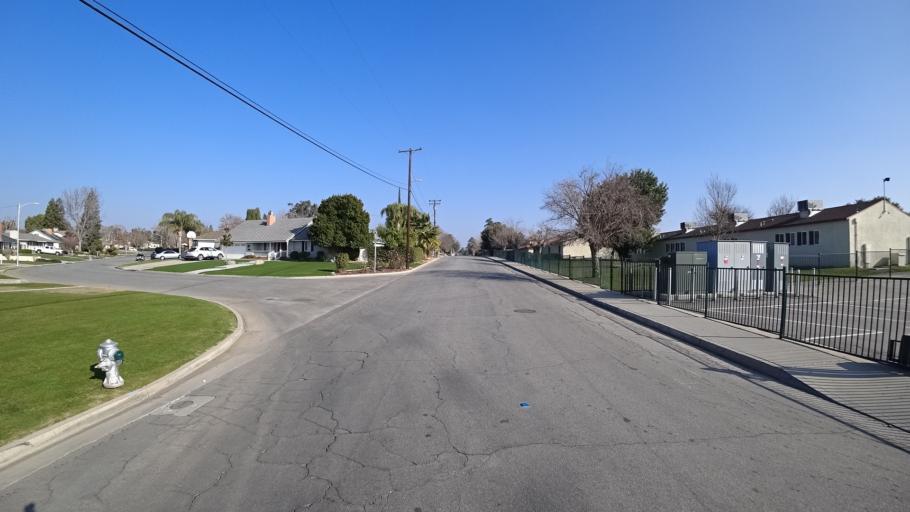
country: US
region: California
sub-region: Kern County
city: Oildale
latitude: 35.4011
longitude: -119.0004
